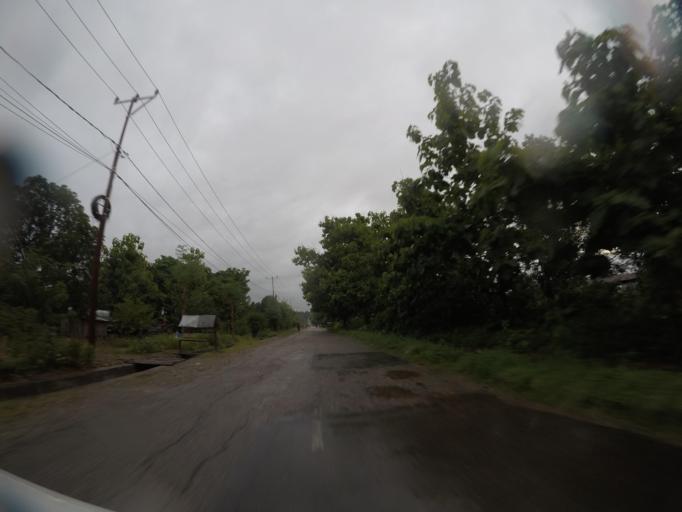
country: TL
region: Bobonaro
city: Maliana
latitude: -8.9616
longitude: 125.1169
